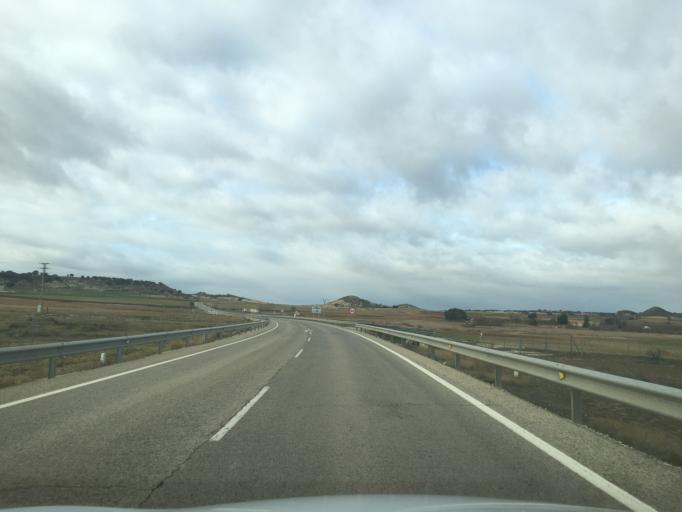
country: ES
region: Castille-La Mancha
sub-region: Provincia de Albacete
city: Petrola
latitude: 38.8303
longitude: -1.5589
